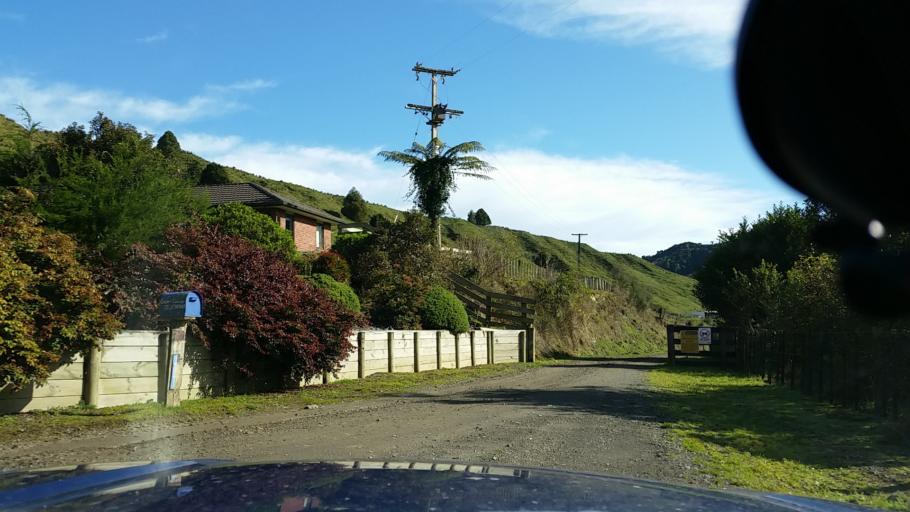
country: NZ
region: Taranaki
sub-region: New Plymouth District
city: Waitara
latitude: -39.0529
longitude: 174.7505
